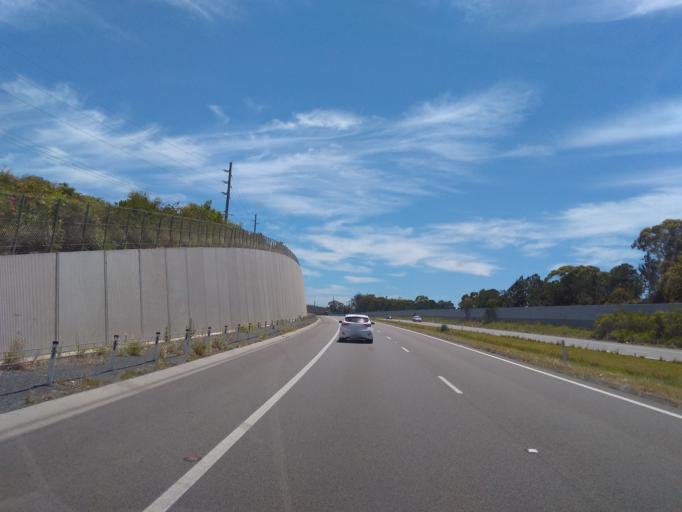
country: AU
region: New South Wales
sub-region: Coffs Harbour
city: Moonee Beach
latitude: -30.2383
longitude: 153.1467
